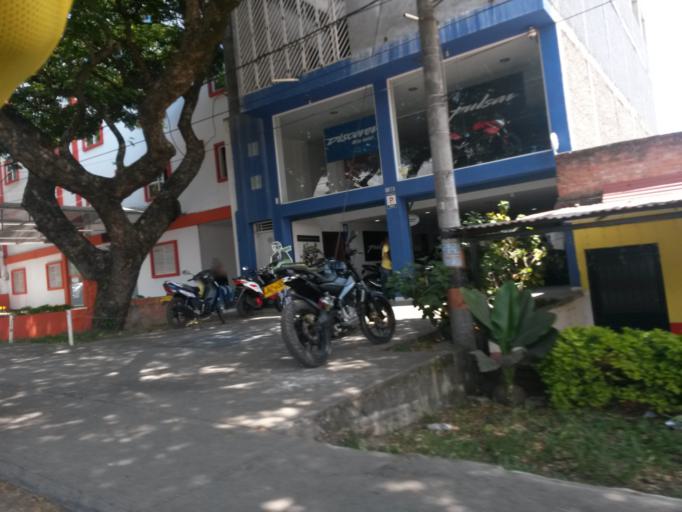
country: CO
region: Cauca
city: Santander de Quilichao
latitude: 3.0152
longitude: -76.4829
